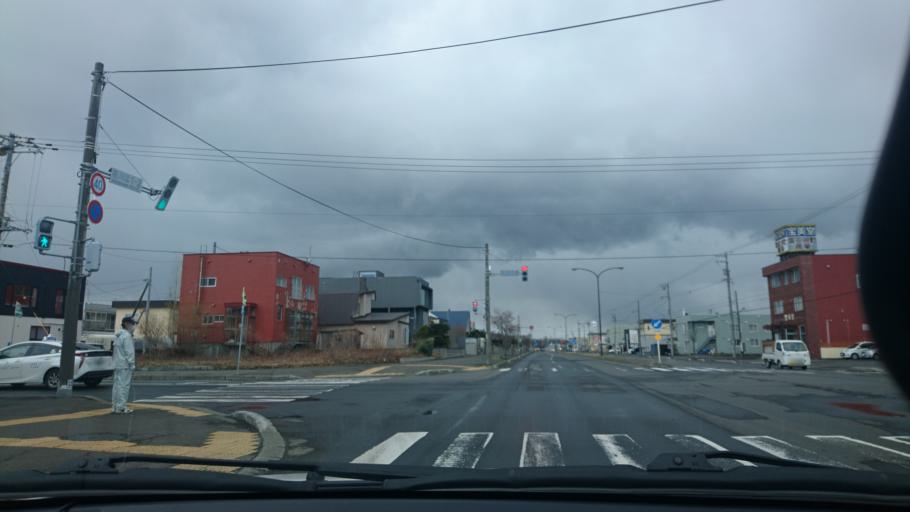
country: JP
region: Hokkaido
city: Ishikari
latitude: 43.1555
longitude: 141.3024
